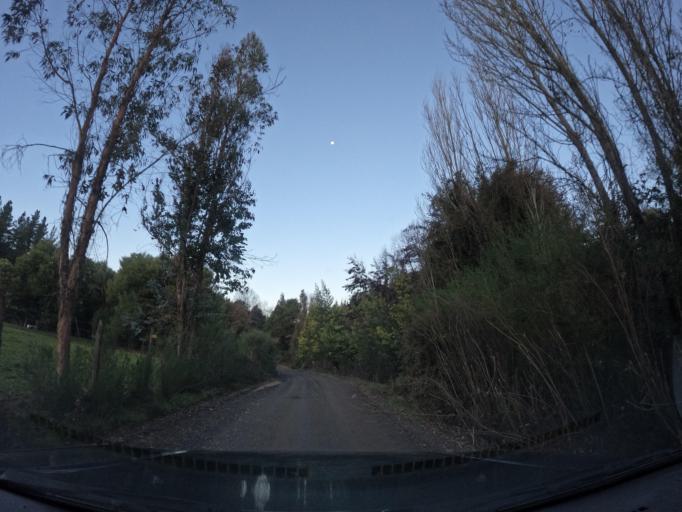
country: CL
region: Biobio
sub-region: Provincia de Concepcion
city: Chiguayante
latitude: -36.9935
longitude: -72.8355
